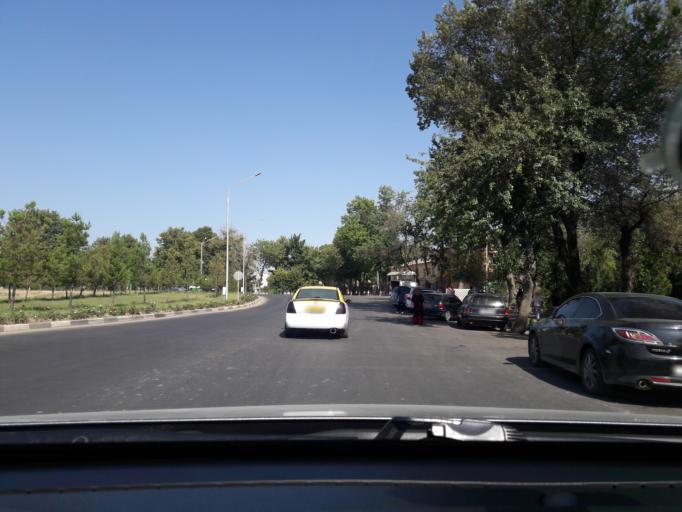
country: TJ
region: Dushanbe
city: Dushanbe
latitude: 38.5692
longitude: 68.7574
